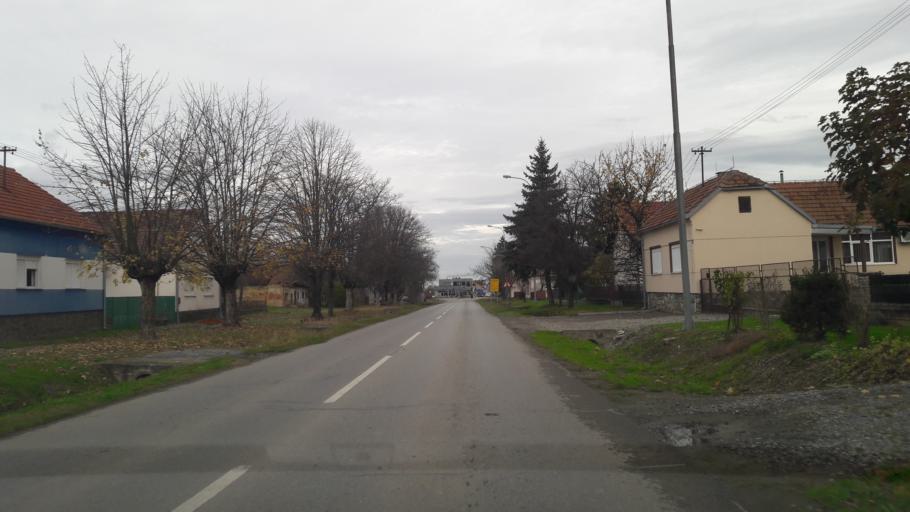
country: HR
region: Virovitick-Podravska
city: Orahovica
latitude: 45.5464
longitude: 17.9010
